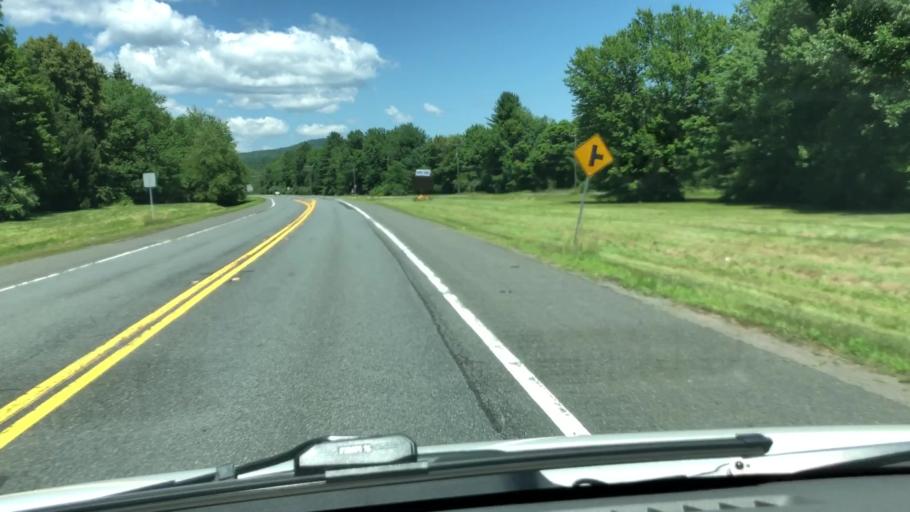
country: US
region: Massachusetts
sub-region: Hampshire County
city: North Amherst
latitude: 42.4202
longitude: -72.5369
